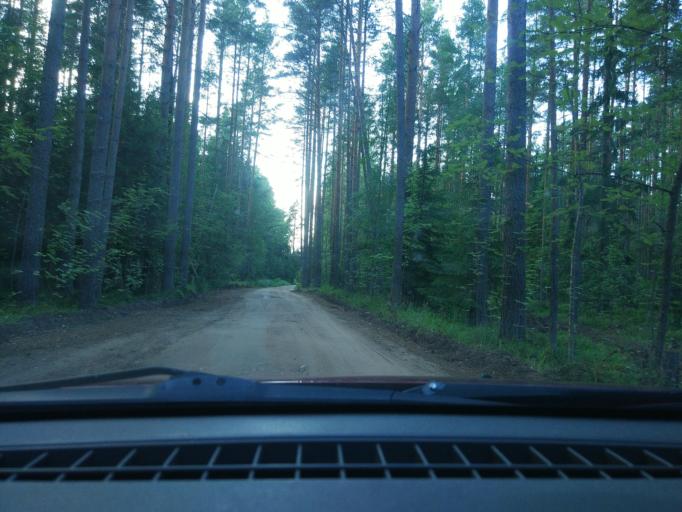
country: RU
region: Leningrad
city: Priozersk
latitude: 60.9315
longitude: 30.0519
